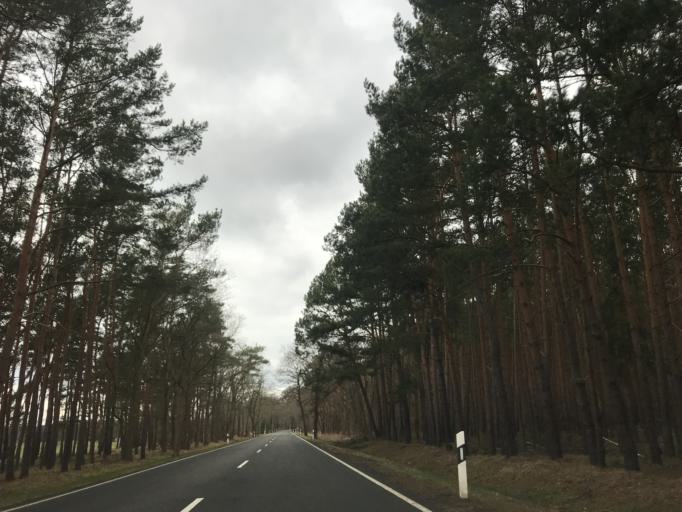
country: DE
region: Brandenburg
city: Kasel-Golzig
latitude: 51.9711
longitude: 13.6709
